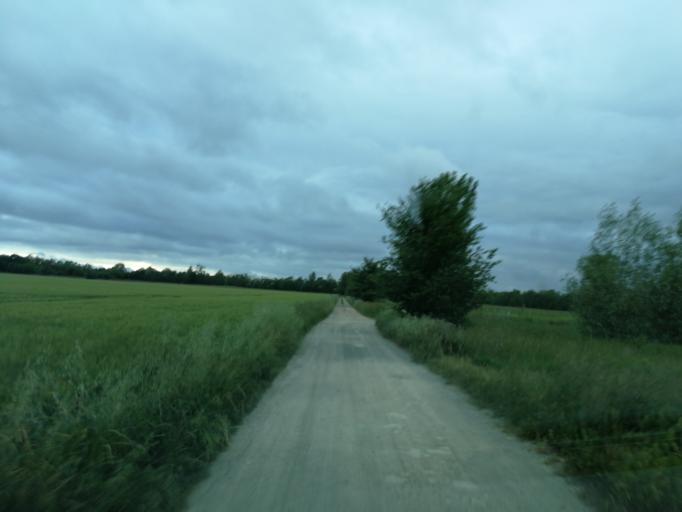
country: FR
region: Poitou-Charentes
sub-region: Departement de la Charente-Maritime
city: Marans
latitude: 46.3578
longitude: -0.9478
